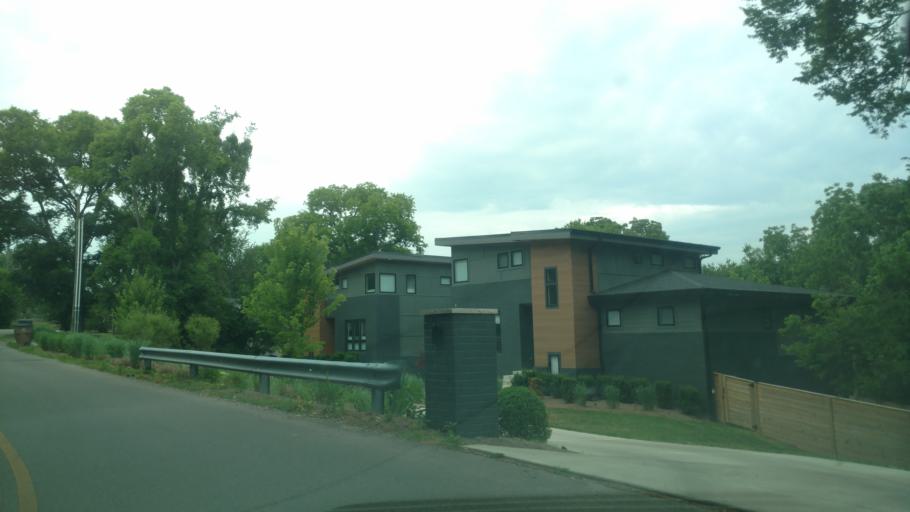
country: US
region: Tennessee
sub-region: Davidson County
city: Nashville
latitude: 36.2012
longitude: -86.7141
